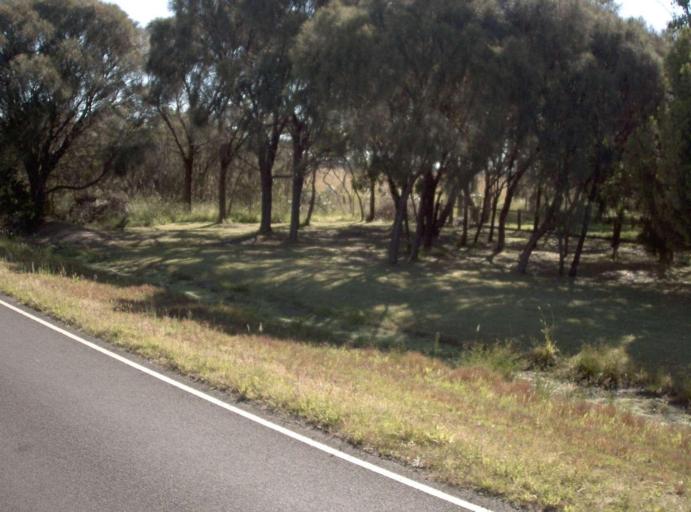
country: AU
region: Victoria
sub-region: Latrobe
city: Traralgon
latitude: -38.6362
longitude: 146.6741
